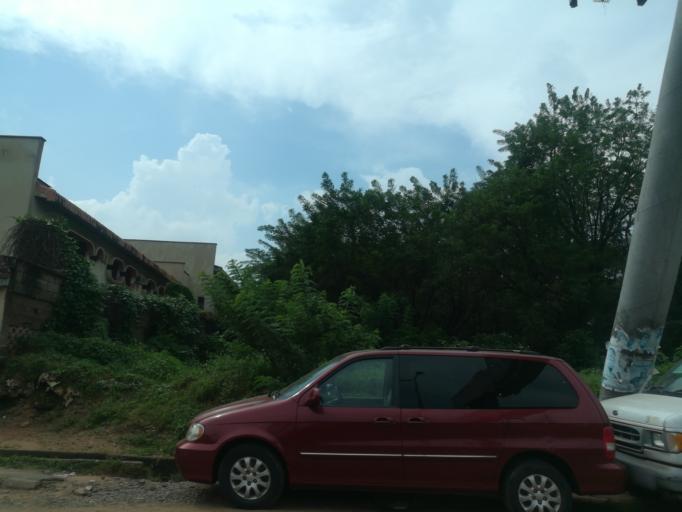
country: NG
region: Oyo
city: Ibadan
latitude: 7.4172
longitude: 3.8964
